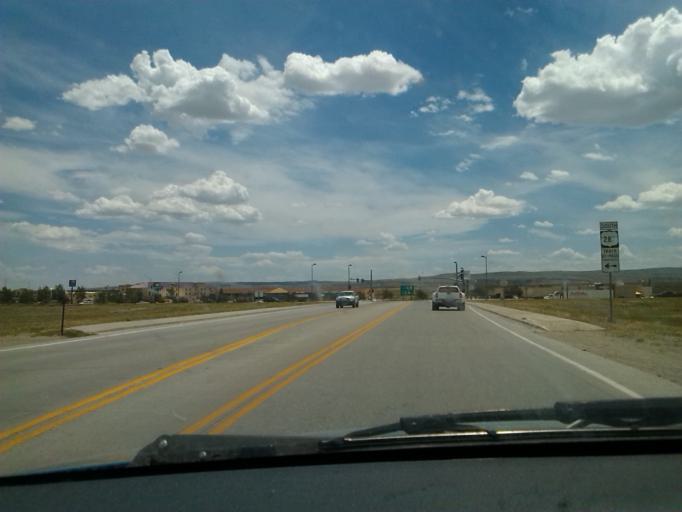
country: US
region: Wyoming
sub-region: Carbon County
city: Rawlins
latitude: 41.7941
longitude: -107.2146
